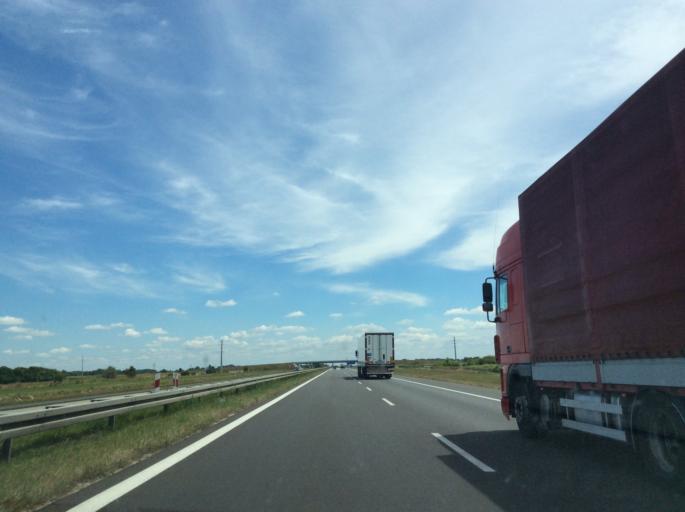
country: PL
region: Greater Poland Voivodeship
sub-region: Powiat poznanski
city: Swarzedz
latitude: 52.3336
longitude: 17.0704
